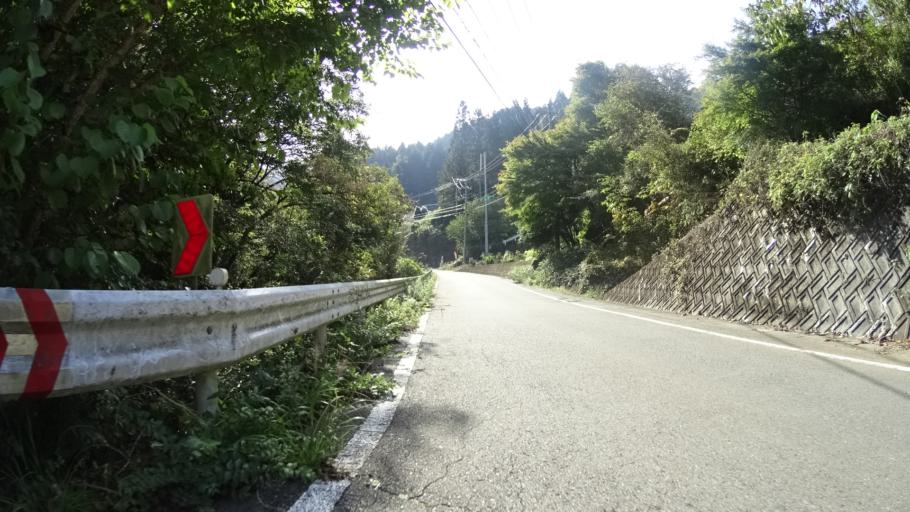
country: JP
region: Yamanashi
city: Otsuki
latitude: 35.5874
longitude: 138.9641
